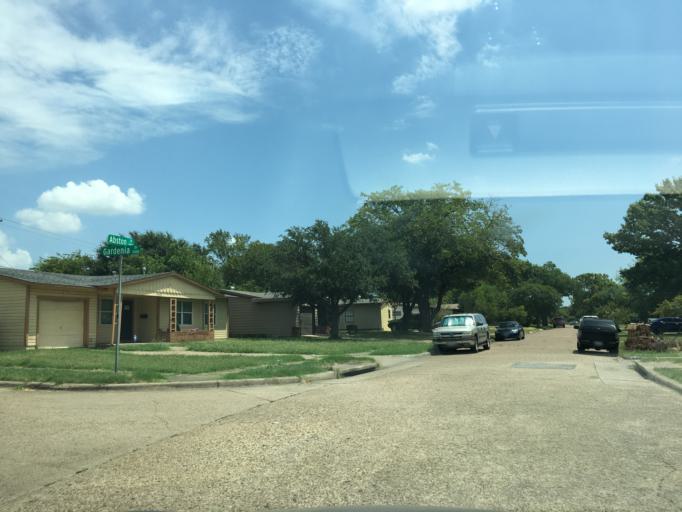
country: US
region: Texas
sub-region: Dallas County
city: Garland
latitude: 32.8626
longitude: -96.6812
